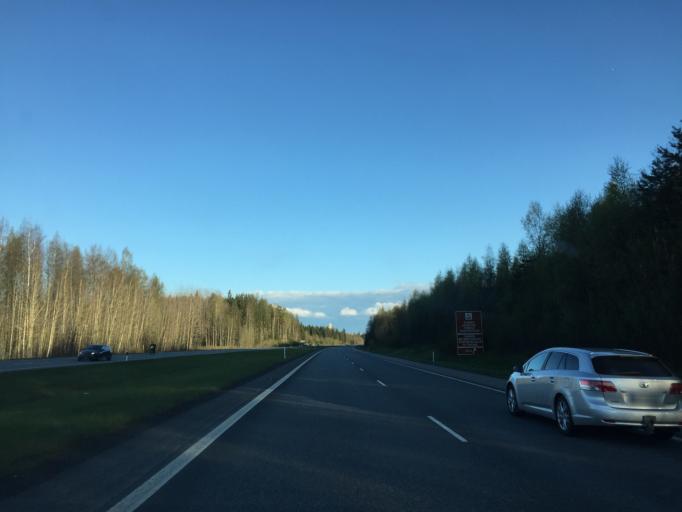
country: FI
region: Haeme
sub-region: Riihimaeki
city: Riihimaeki
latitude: 60.7635
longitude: 24.7226
